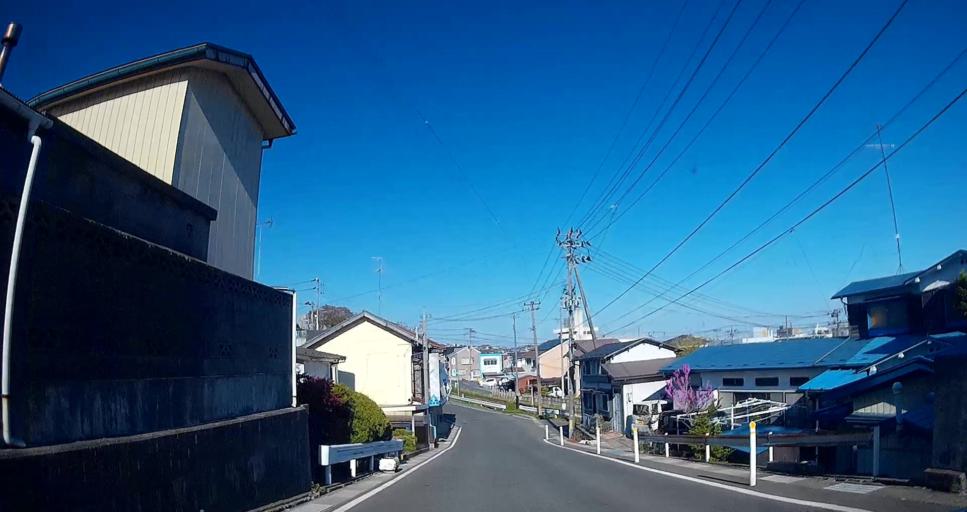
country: JP
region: Aomori
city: Hachinohe
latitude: 40.5222
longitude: 141.5444
